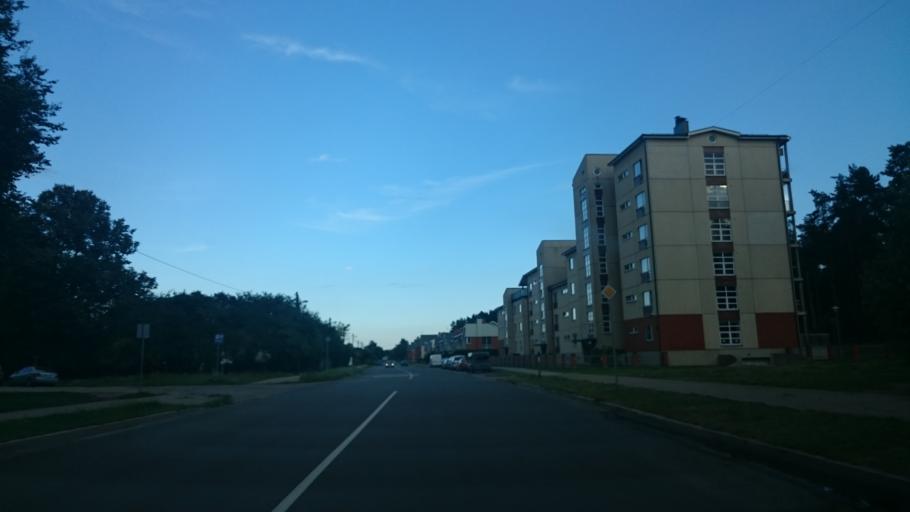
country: LV
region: Riga
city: Bergi
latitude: 56.9865
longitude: 24.2319
